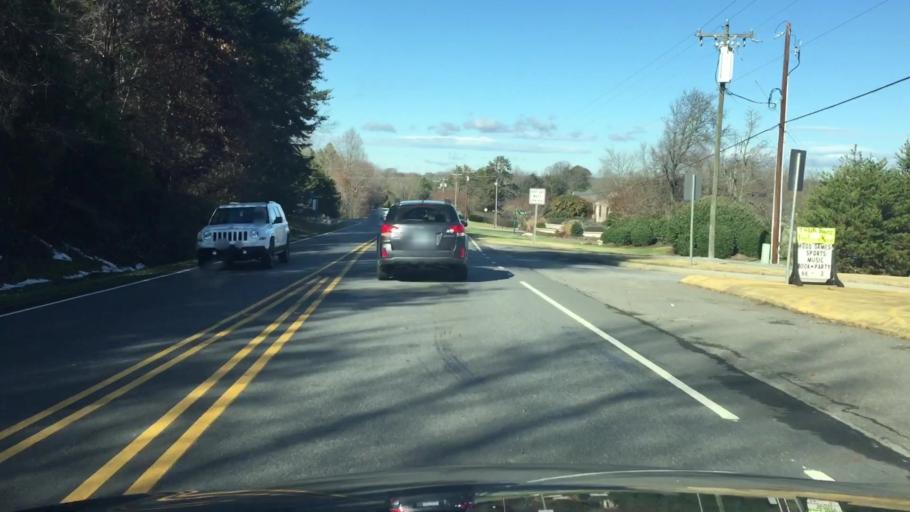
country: US
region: North Carolina
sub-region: Iredell County
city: Mooresville
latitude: 35.5581
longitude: -80.8629
